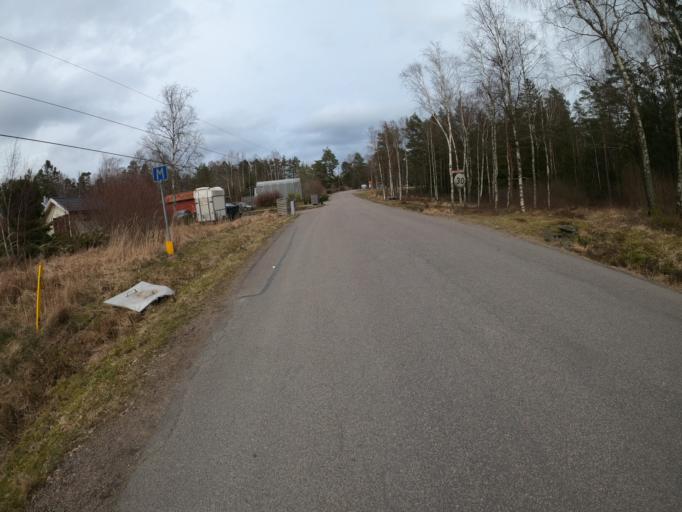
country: SE
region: Vaestra Goetaland
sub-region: Harryda Kommun
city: Molnlycke
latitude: 57.6179
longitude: 12.1040
